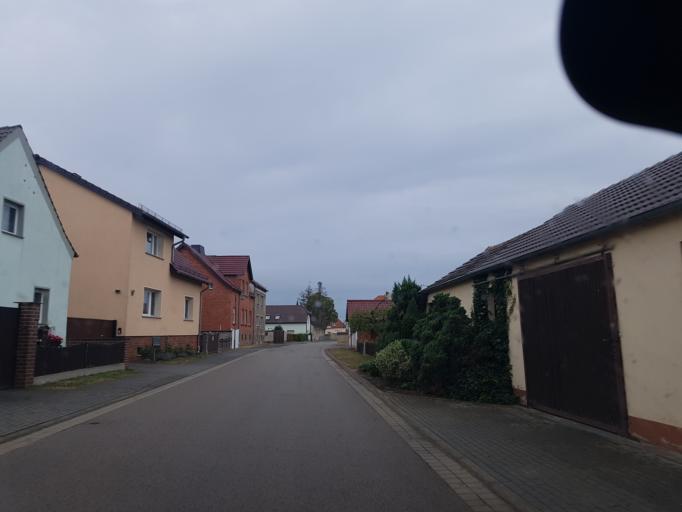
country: DE
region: Saxony-Anhalt
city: Elster
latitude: 51.7975
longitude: 12.8703
